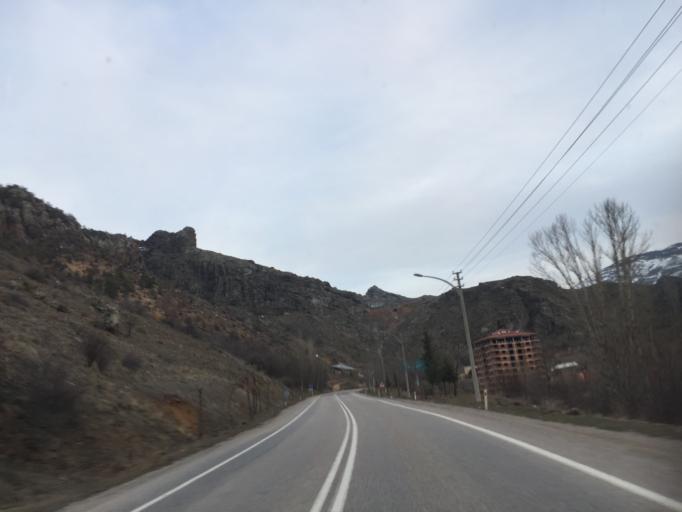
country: TR
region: Gumushane
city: Gumushkhane
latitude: 40.4763
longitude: 39.4618
